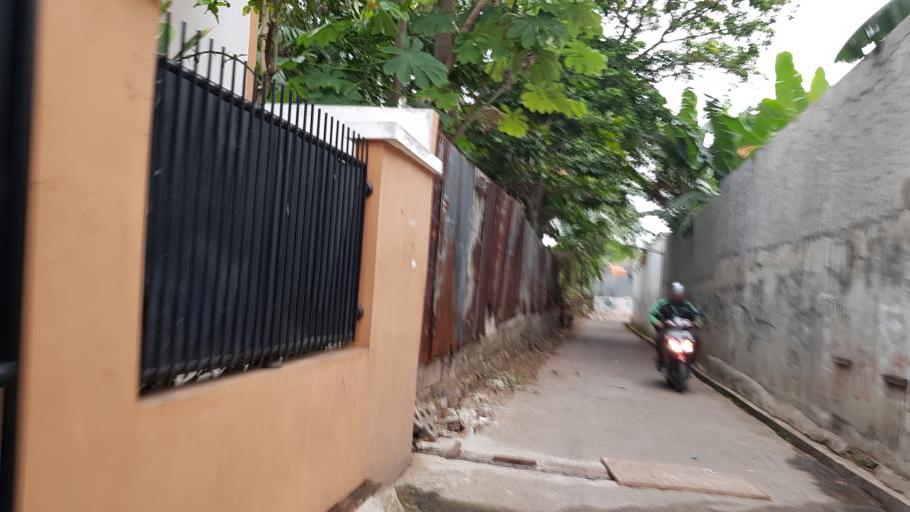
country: ID
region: West Java
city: Pamulang
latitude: -6.3411
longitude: 106.7895
